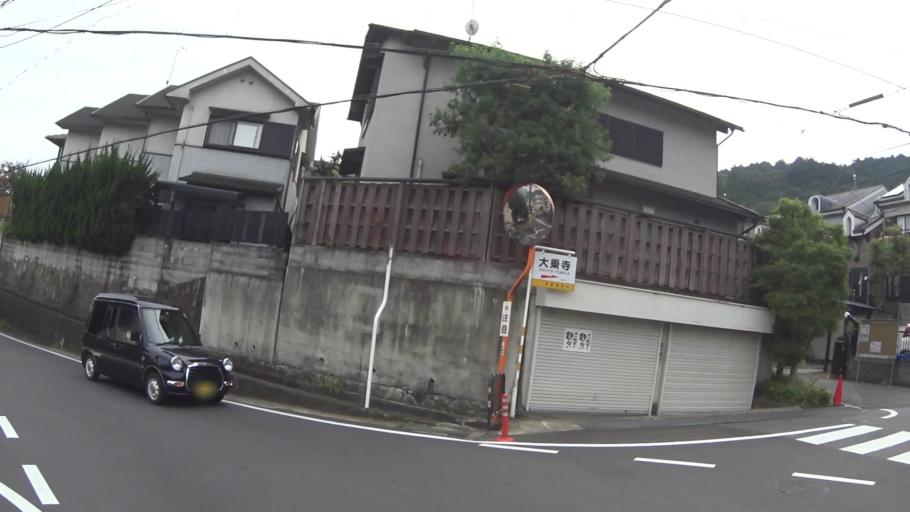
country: JP
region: Kyoto
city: Kyoto
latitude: 34.9947
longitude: 135.7999
